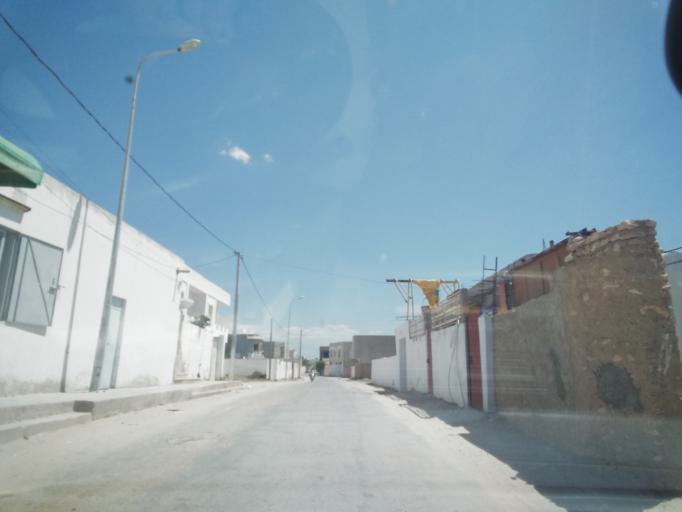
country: TN
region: Safaqis
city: Al Qarmadah
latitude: 34.8226
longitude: 10.7682
